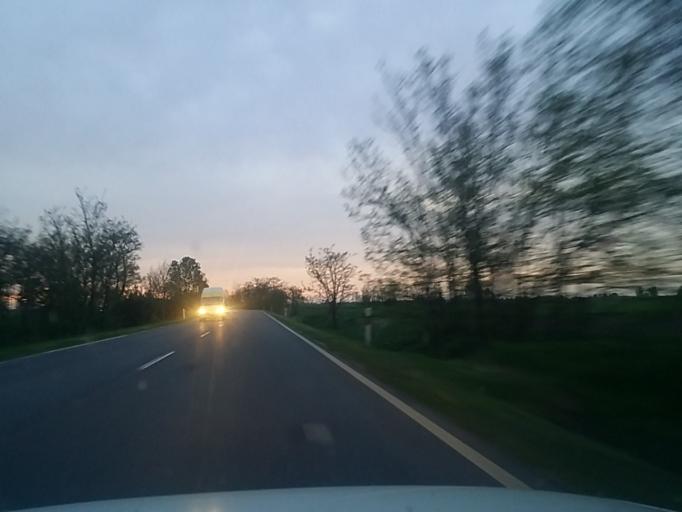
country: HU
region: Bekes
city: Csorvas
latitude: 46.7250
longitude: 20.9220
